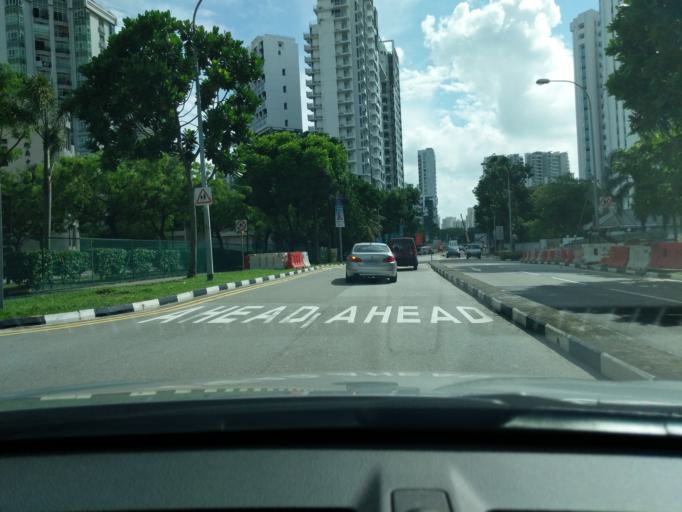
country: SG
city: Singapore
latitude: 1.2981
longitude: 103.8829
